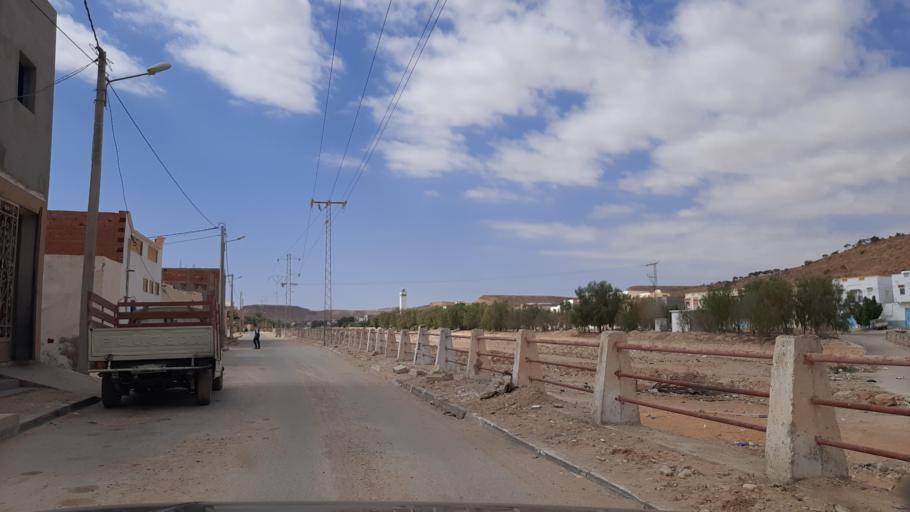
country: TN
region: Tataouine
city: Tataouine
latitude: 32.9330
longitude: 10.4470
